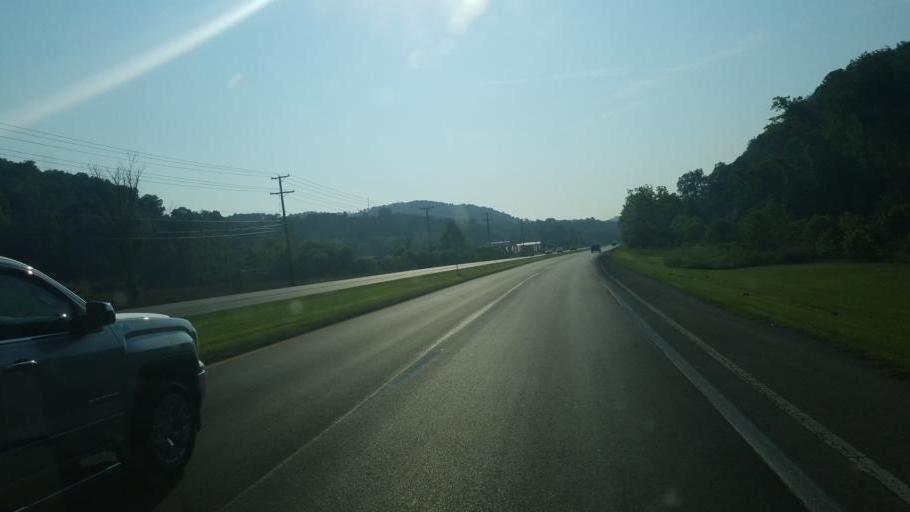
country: US
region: Tennessee
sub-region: Sullivan County
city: Bloomingdale
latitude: 36.5751
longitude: -82.4224
